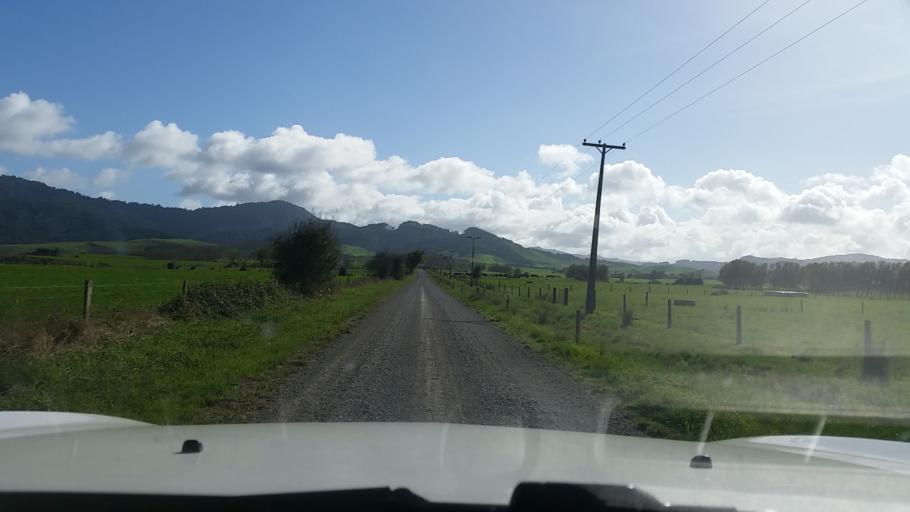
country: NZ
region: Waikato
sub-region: Hauraki District
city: Ngatea
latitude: -37.5136
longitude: 175.4096
